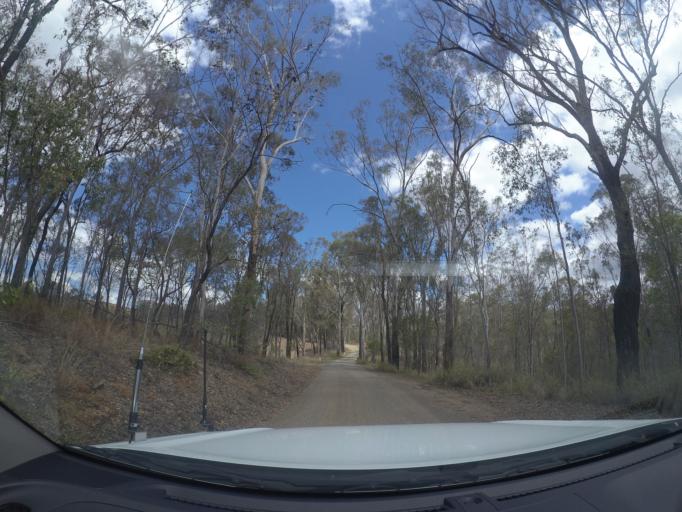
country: AU
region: Queensland
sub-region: Logan
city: Cedar Vale
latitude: -27.8899
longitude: 153.0439
